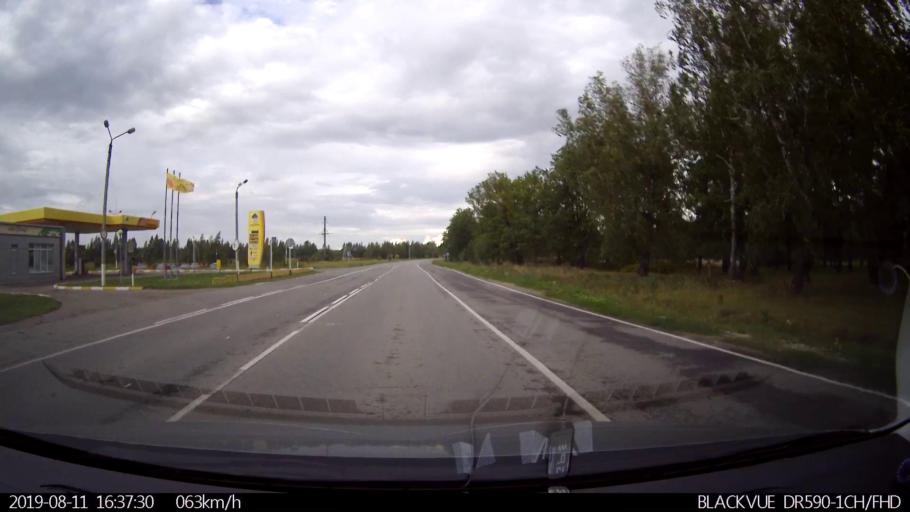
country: RU
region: Ulyanovsk
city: Mayna
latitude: 54.1278
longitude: 47.6148
